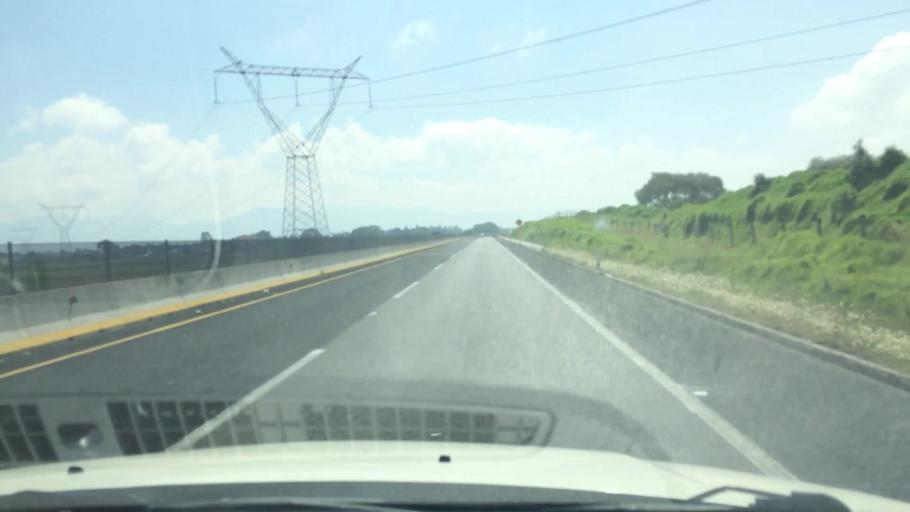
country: MX
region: Mexico
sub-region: Otzolotepec
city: La Y
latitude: 19.4013
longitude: -99.5844
